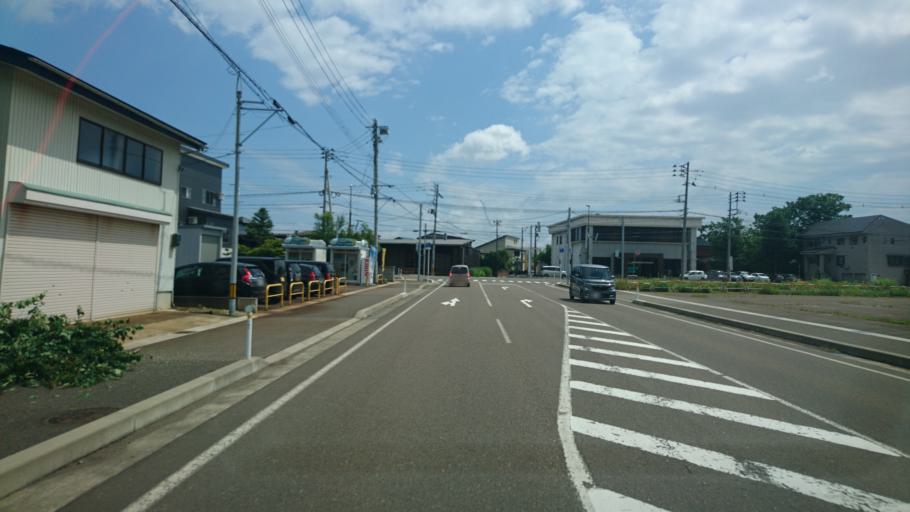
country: JP
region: Niigata
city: Joetsu
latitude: 37.0792
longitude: 138.2514
